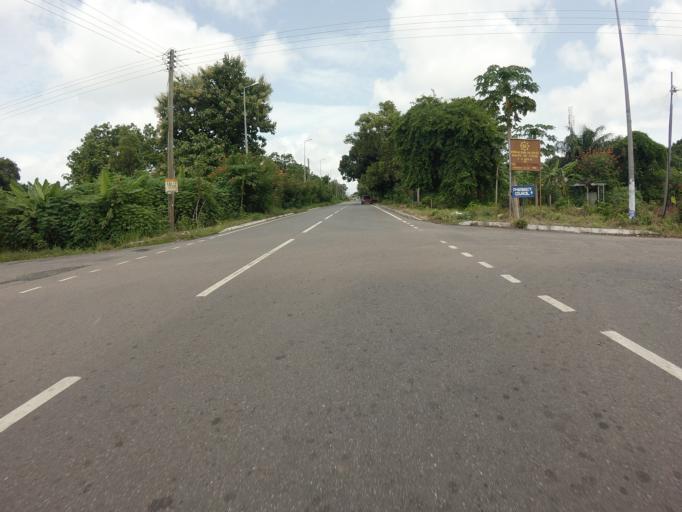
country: GH
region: Volta
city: Ho
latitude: 6.6066
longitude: 0.4613
